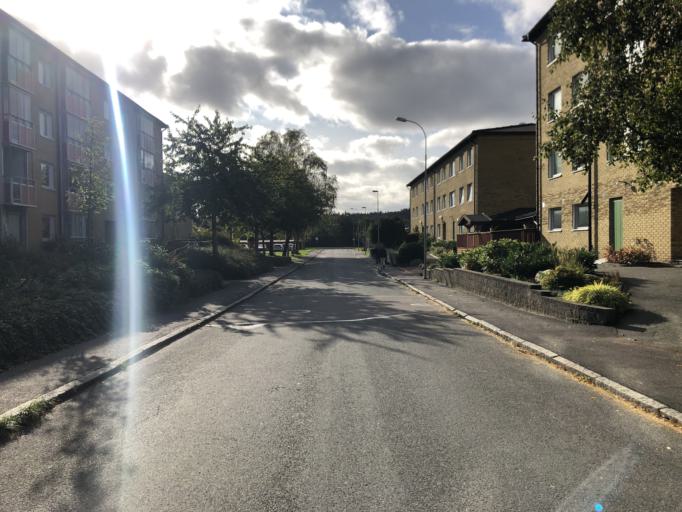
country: SE
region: Vaestra Goetaland
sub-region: Molndal
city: Moelndal
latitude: 57.6463
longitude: 12.0096
